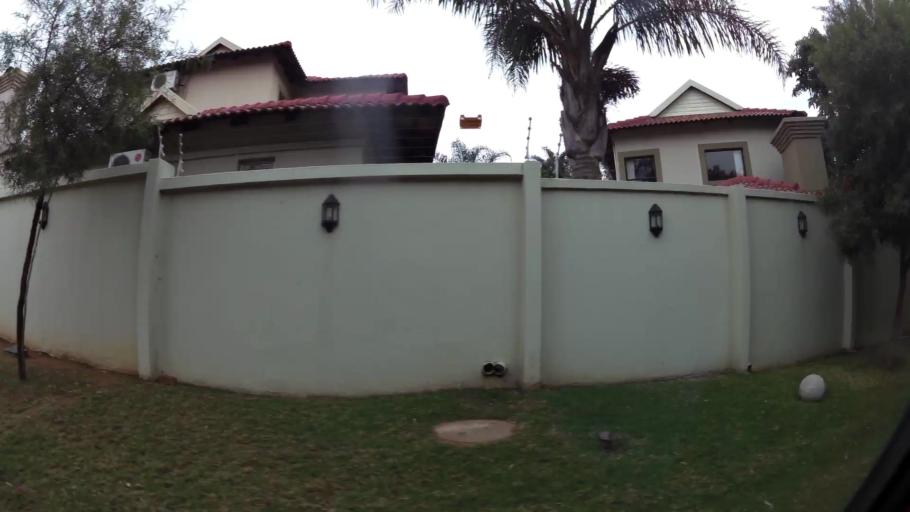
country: ZA
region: Gauteng
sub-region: City of Johannesburg Metropolitan Municipality
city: Roodepoort
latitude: -26.1151
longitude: 27.9082
